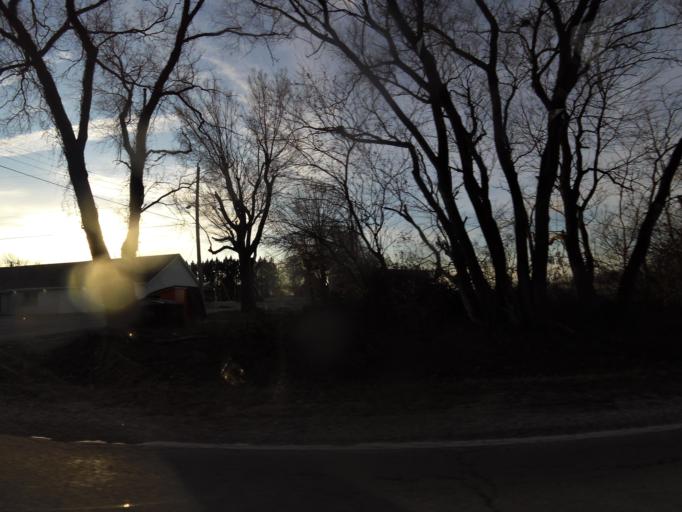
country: US
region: Illinois
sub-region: Fayette County
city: Vandalia
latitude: 38.9558
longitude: -89.1232
